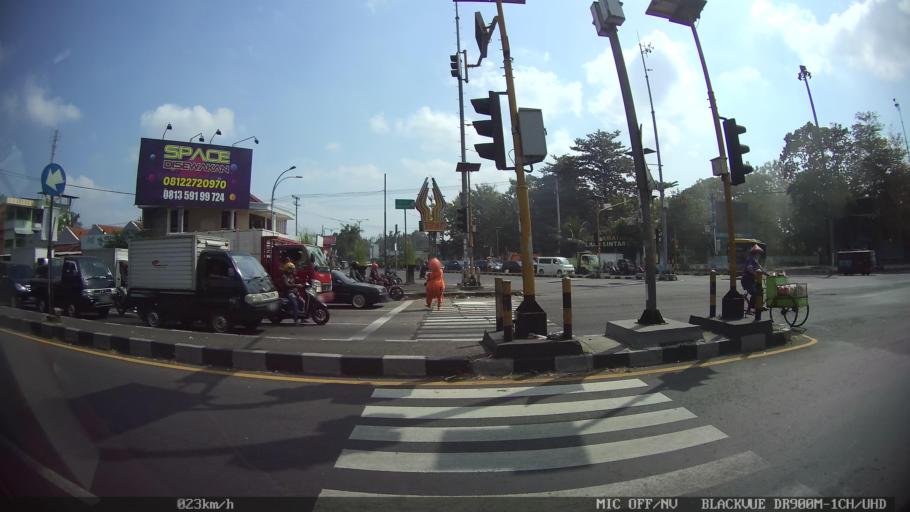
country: ID
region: Daerah Istimewa Yogyakarta
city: Sewon
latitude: -7.8360
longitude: 110.3925
